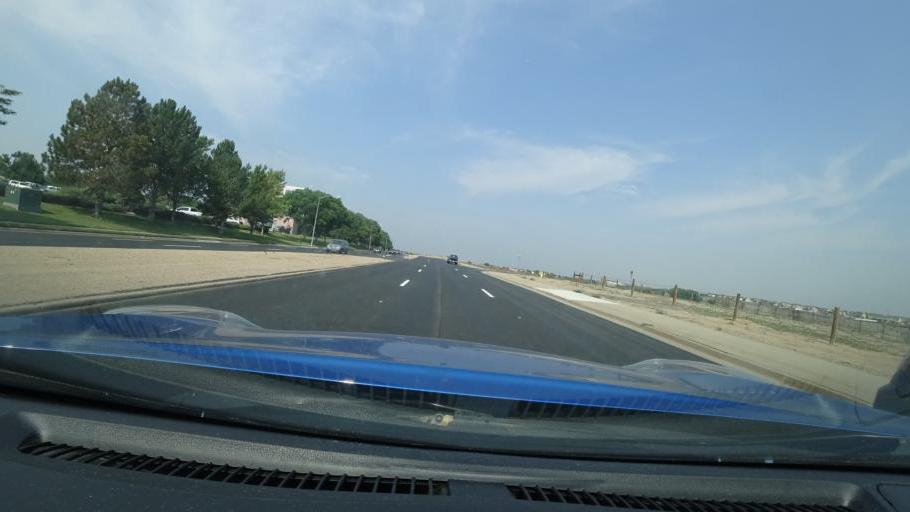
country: US
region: Colorado
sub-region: Adams County
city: Aurora
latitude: 39.7058
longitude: -104.7824
